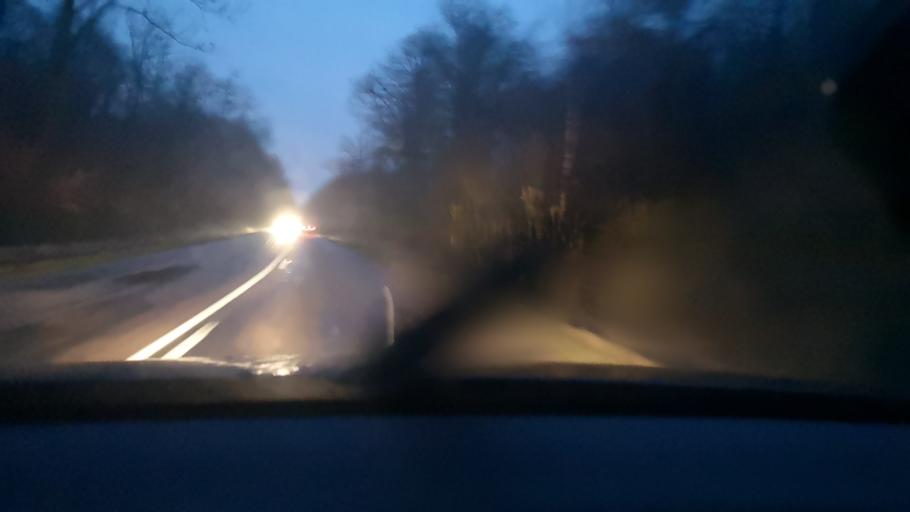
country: FR
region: Bourgogne
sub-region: Departement de Saone-et-Loire
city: Virey-le-Grand
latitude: 46.8778
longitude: 4.8513
